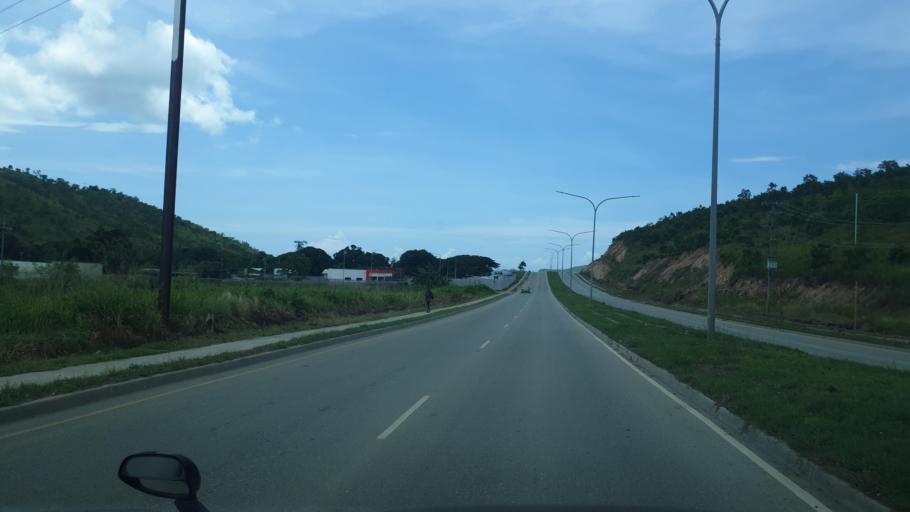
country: PG
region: National Capital
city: Port Moresby
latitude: -9.4318
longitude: 147.1410
